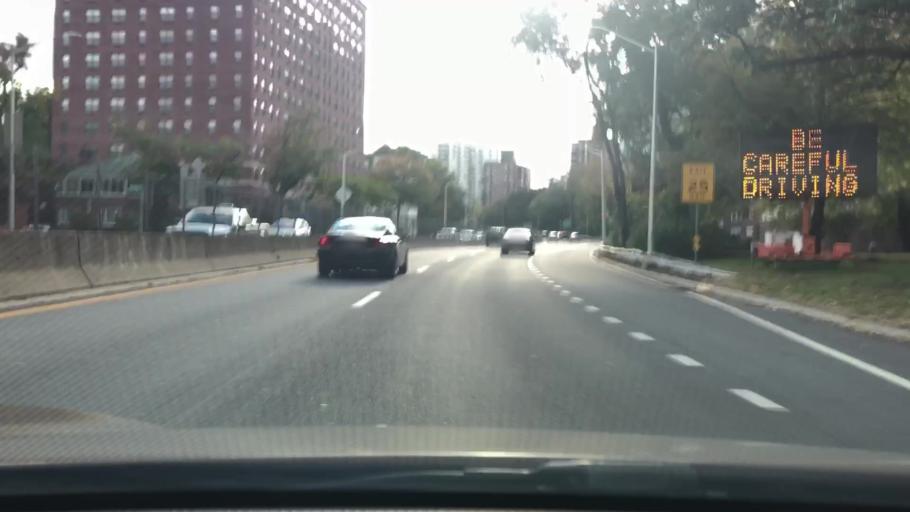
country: US
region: New York
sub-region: New York County
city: Inwood
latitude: 40.8891
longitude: -73.9092
